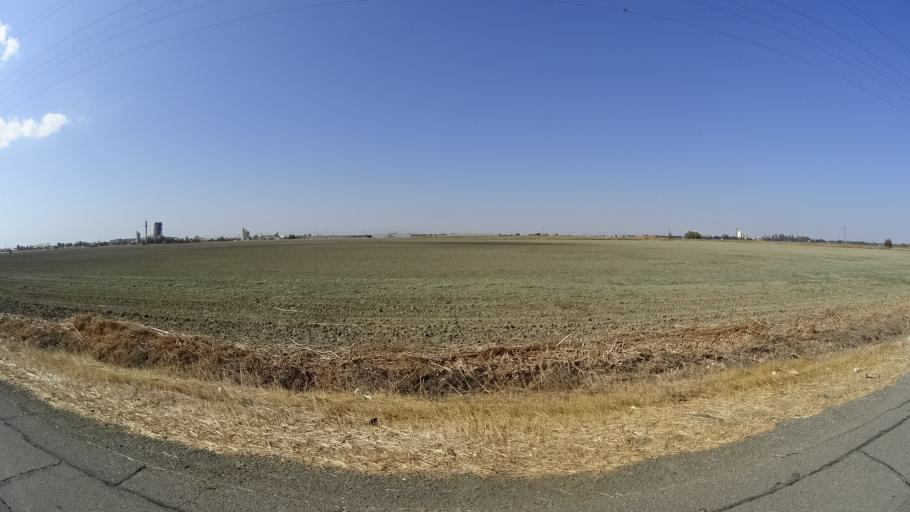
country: US
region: California
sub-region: Yolo County
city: Woodland
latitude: 38.6964
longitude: -121.7282
